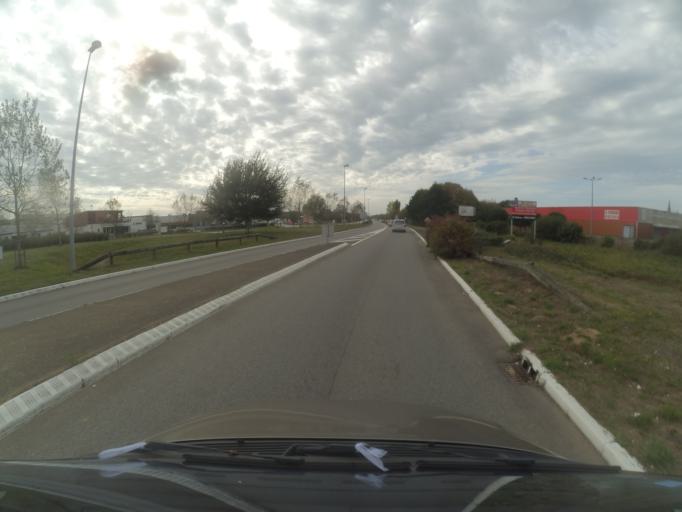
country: FR
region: Brittany
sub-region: Departement du Morbihan
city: Merlevenez
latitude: 47.7385
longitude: -3.2266
